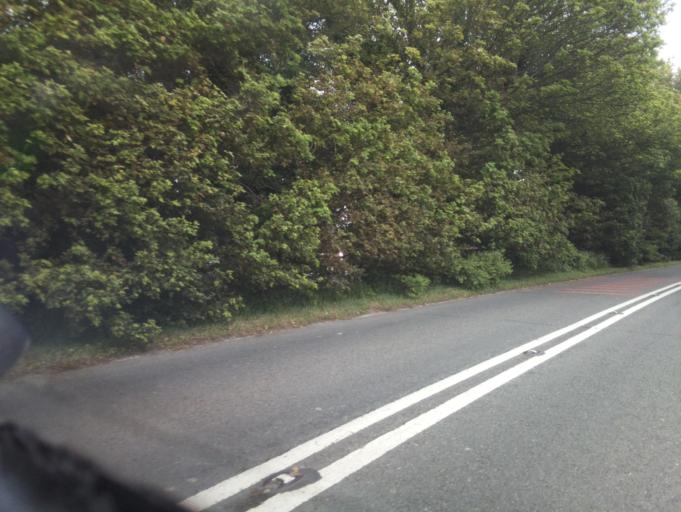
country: GB
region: Wales
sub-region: Vale of Glamorgan
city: Rhoose
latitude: 51.3992
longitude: -3.4173
